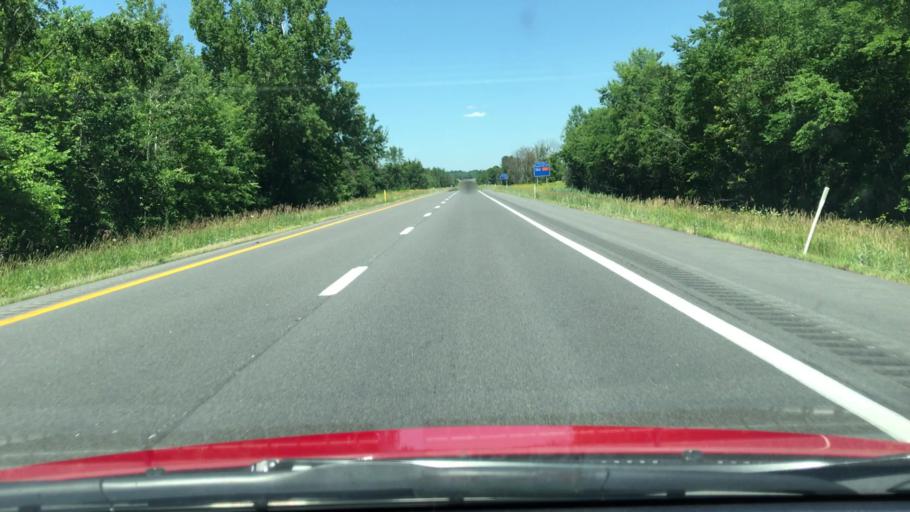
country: US
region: New York
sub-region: Clinton County
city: Cumberland Head
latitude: 44.7678
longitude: -73.4326
